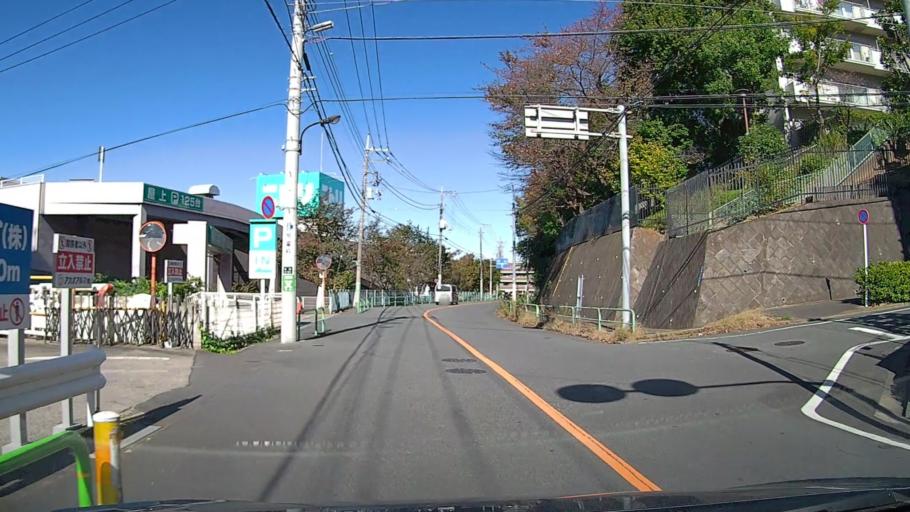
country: JP
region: Saitama
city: Wako
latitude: 35.7777
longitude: 139.6254
